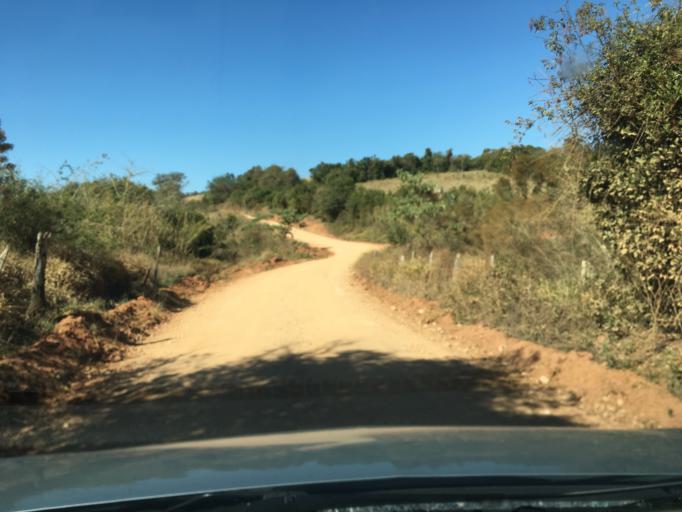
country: BR
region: Minas Gerais
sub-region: Campestre
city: Campestre
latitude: -21.5692
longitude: -46.1979
